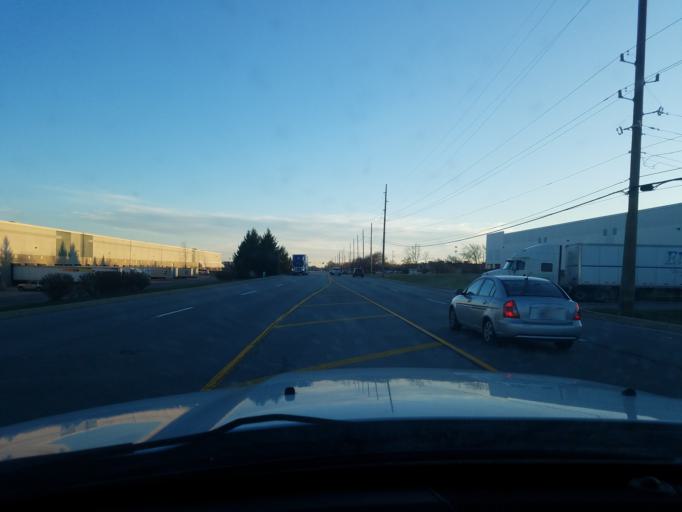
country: US
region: Indiana
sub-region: Boone County
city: Zionsville
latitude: 39.8906
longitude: -86.2598
